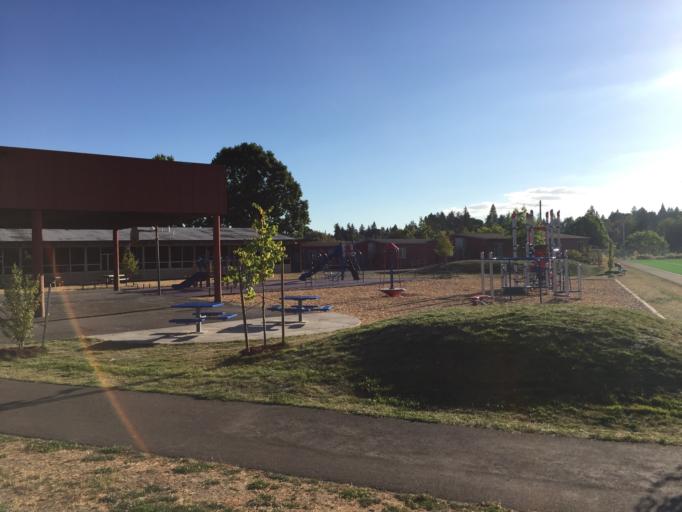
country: US
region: Oregon
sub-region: Multnomah County
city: Portland
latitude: 45.4771
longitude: -122.6951
